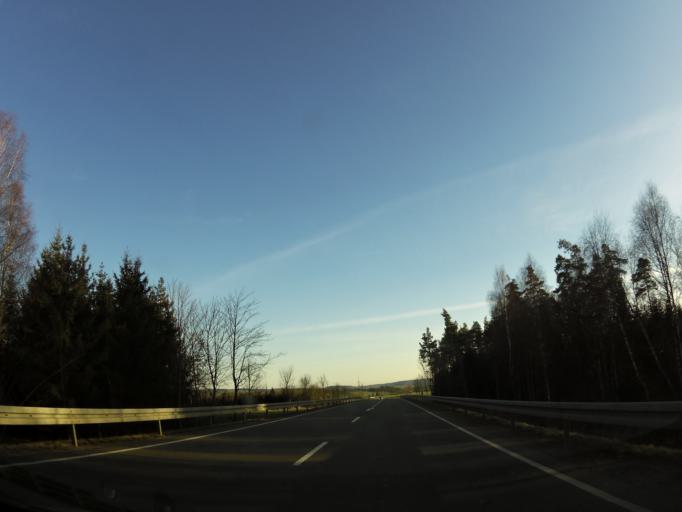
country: DE
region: Thuringia
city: Pormitz
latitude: 50.6297
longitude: 11.8143
